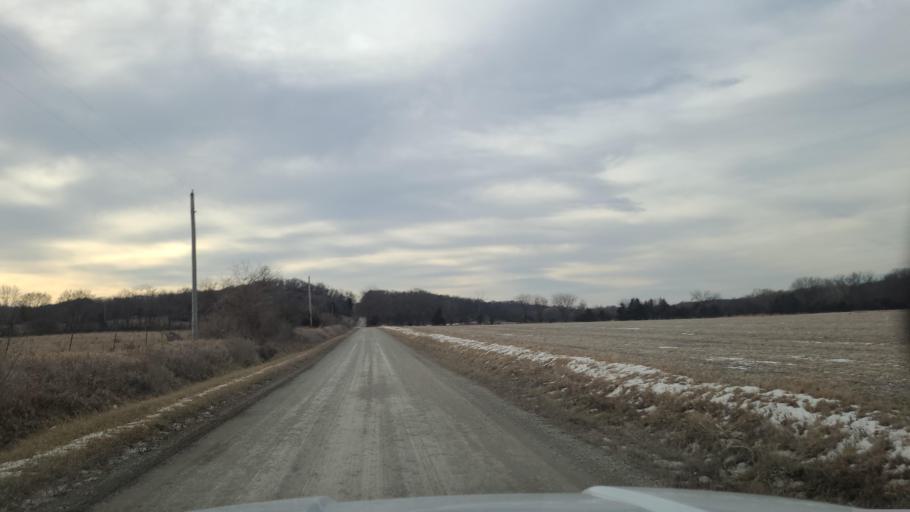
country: US
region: Kansas
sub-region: Shawnee County
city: Topeka
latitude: 39.0537
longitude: -95.4738
